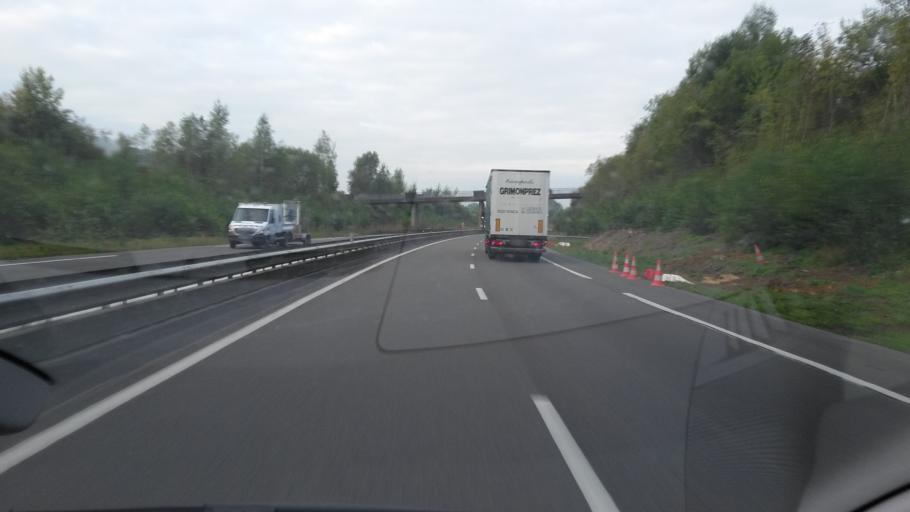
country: FR
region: Champagne-Ardenne
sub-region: Departement des Ardennes
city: La Francheville
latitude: 49.6981
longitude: 4.6923
